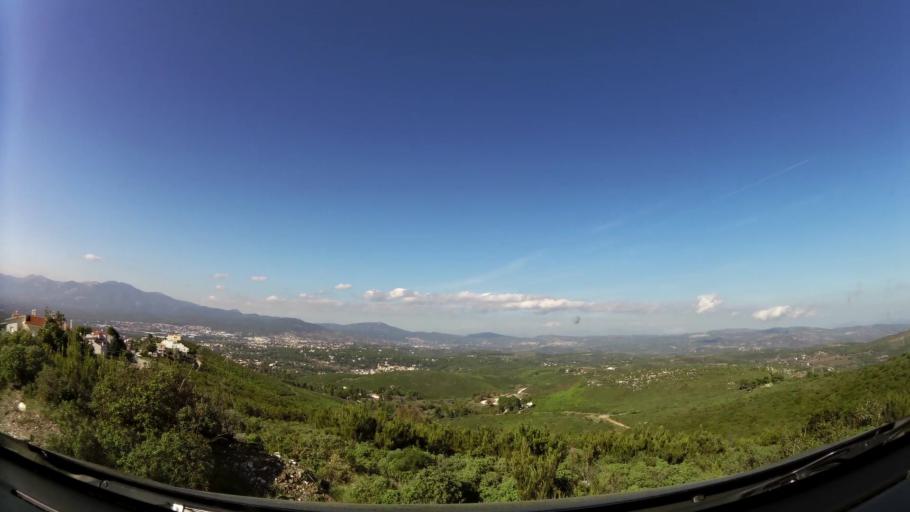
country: GR
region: Attica
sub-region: Nomarchia Anatolikis Attikis
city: Dionysos
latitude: 38.1070
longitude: 23.8922
